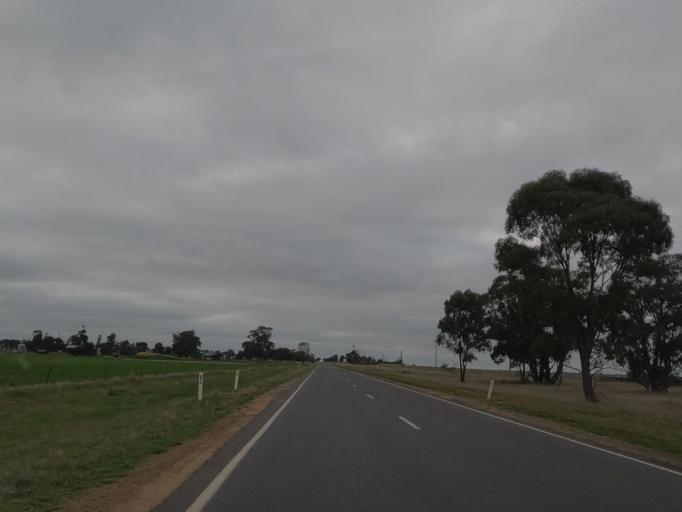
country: AU
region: Victoria
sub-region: Greater Bendigo
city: Long Gully
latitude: -36.5203
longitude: 143.9480
